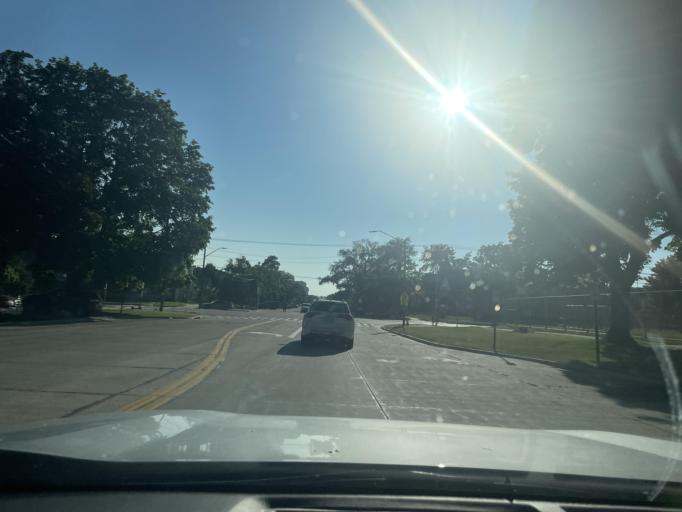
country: US
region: Utah
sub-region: Salt Lake County
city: Salt Lake City
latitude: 40.7585
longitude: -111.8673
